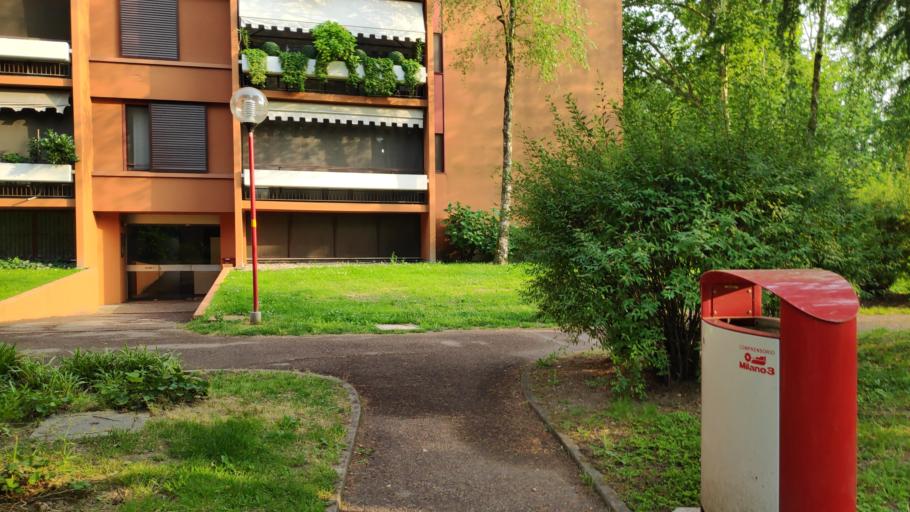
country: IT
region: Lombardy
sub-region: Citta metropolitana di Milano
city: Basiglio
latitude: 45.3625
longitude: 9.1625
